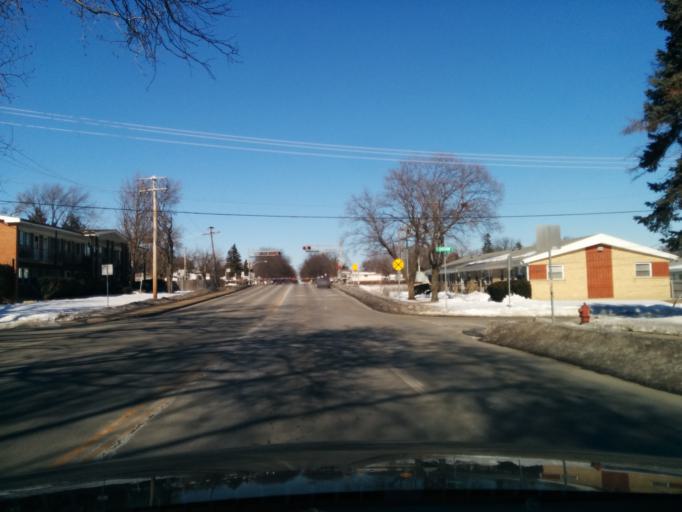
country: US
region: Illinois
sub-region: DuPage County
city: Villa Park
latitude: 41.8942
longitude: -87.9887
